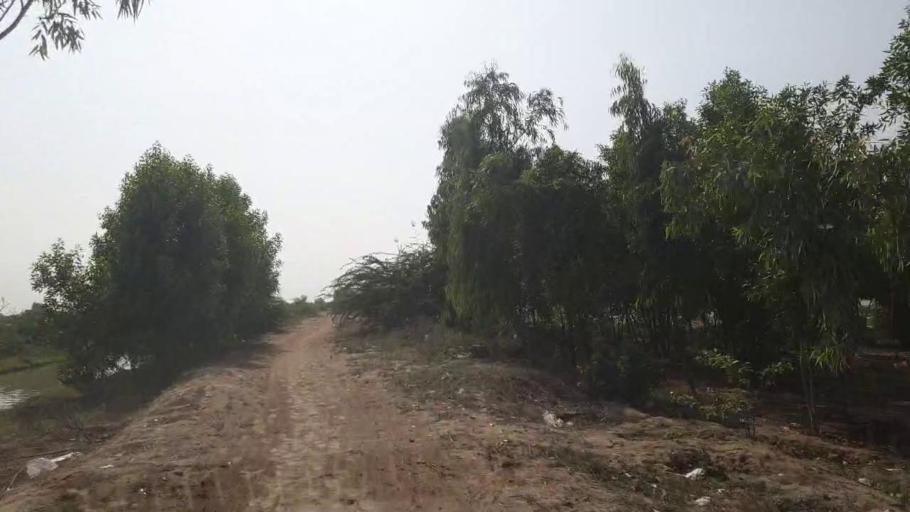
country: PK
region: Sindh
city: Kadhan
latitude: 24.5042
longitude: 68.8499
